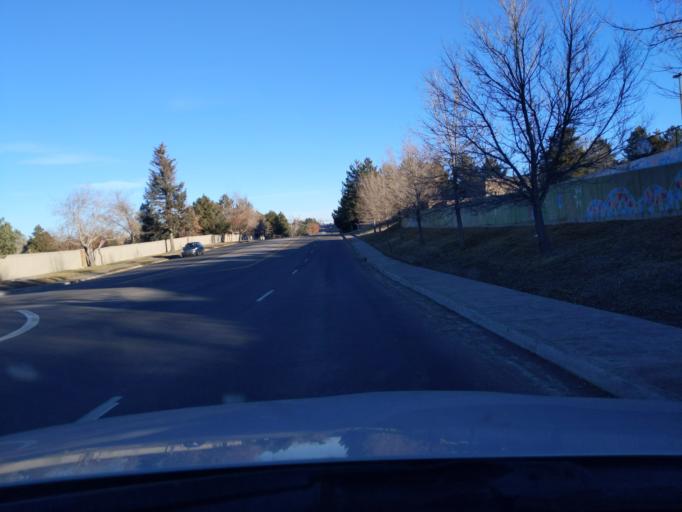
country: US
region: Colorado
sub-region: Arapahoe County
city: Centennial
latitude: 39.5736
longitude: -104.8856
